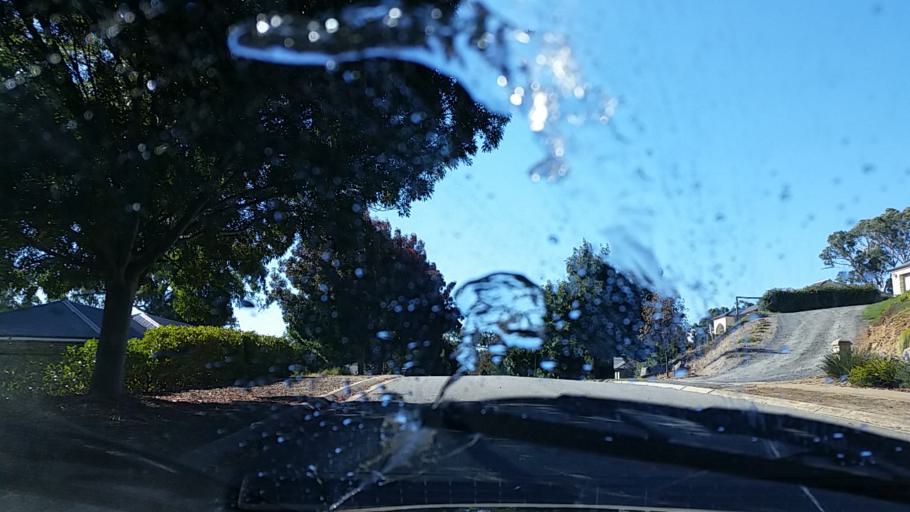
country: AU
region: South Australia
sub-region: Mount Barker
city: Mount Barker
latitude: -35.0644
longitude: 138.8770
